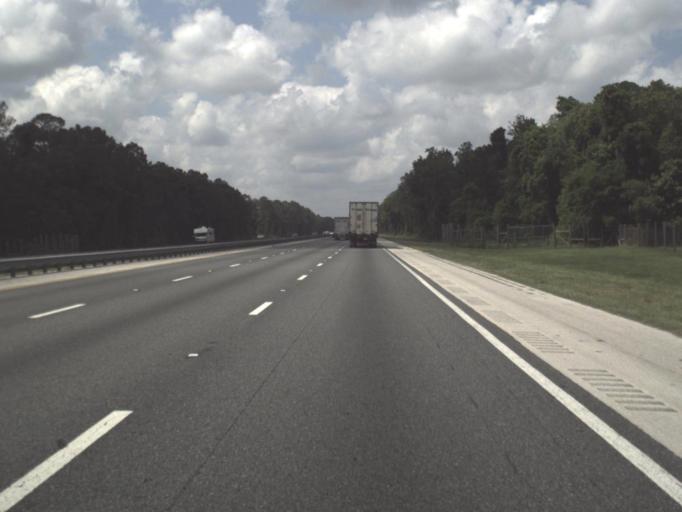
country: US
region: Florida
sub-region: Saint Johns County
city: Saint Augustine South
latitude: 29.8685
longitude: -81.3970
